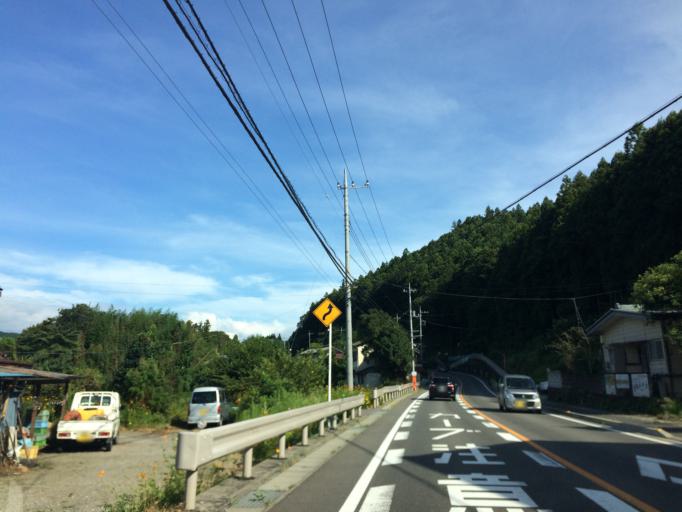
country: JP
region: Gunma
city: Nakanojomachi
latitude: 36.5503
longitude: 138.9084
